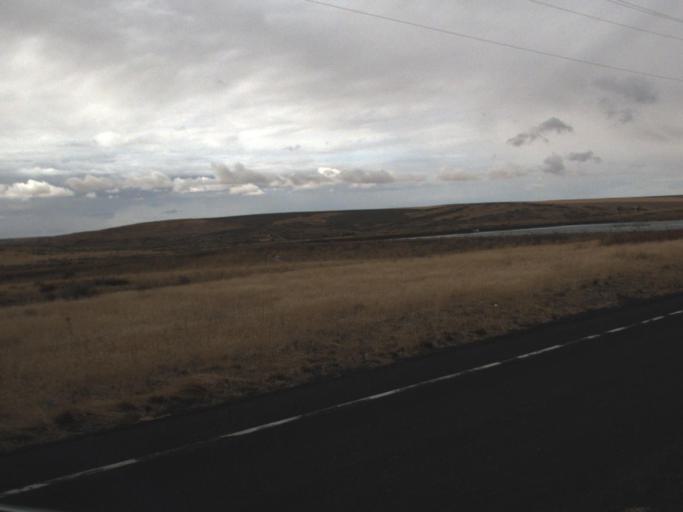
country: US
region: Washington
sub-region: Okanogan County
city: Coulee Dam
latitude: 47.7125
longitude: -118.9202
